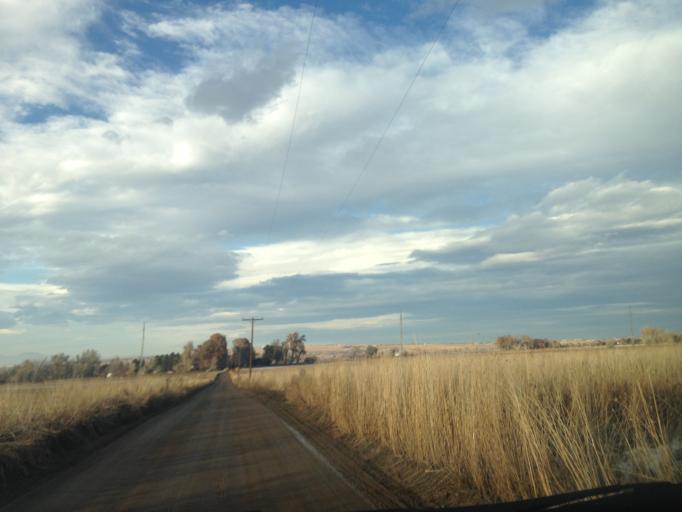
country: US
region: Colorado
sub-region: Boulder County
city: Louisville
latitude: 40.0159
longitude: -105.1594
